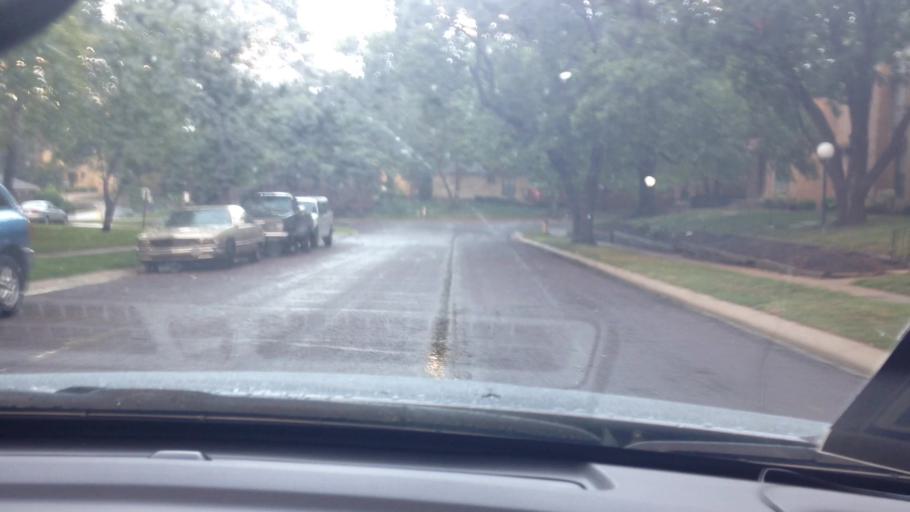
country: US
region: Kansas
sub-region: Johnson County
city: Overland Park
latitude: 38.9436
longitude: -94.6900
